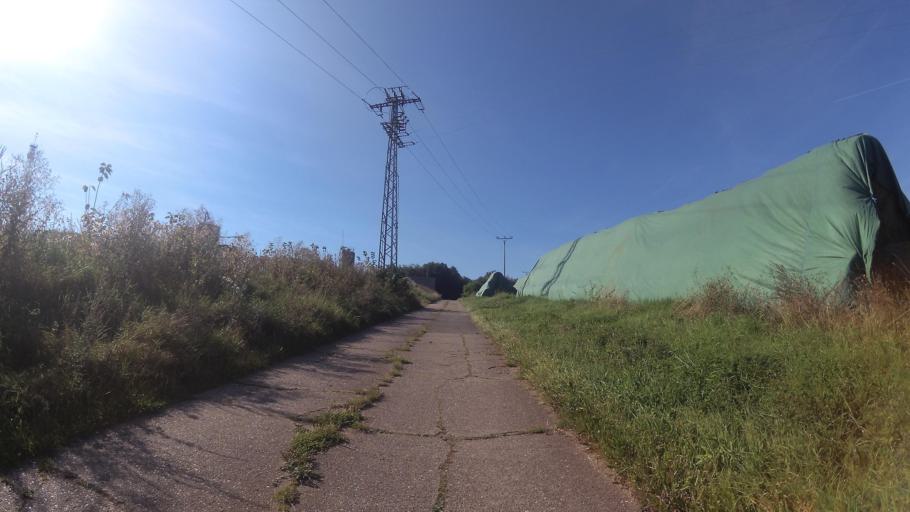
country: DE
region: Rheinland-Pfalz
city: Dunzweiler
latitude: 49.4182
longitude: 7.2937
